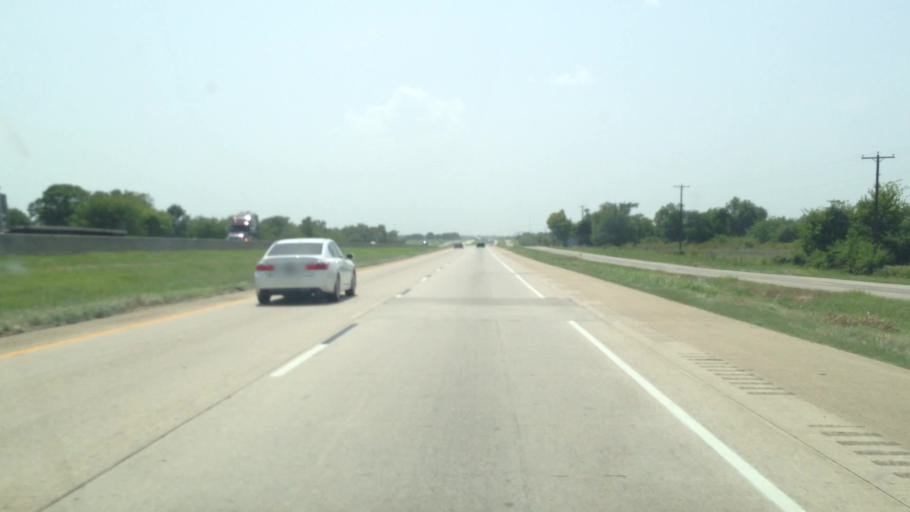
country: US
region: Texas
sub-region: Hopkins County
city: Sulphur Springs
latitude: 33.1209
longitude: -95.6865
